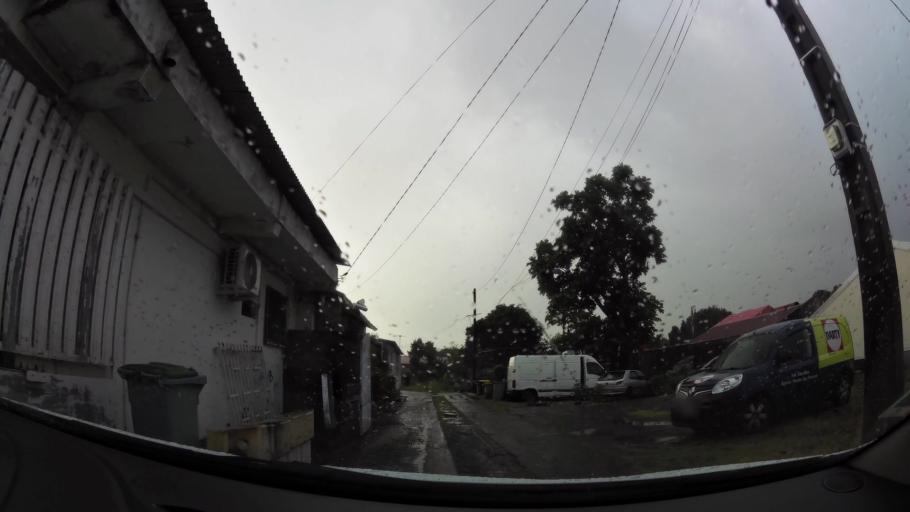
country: RE
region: Reunion
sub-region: Reunion
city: Saint-Andre
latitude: -20.9560
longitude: 55.6676
